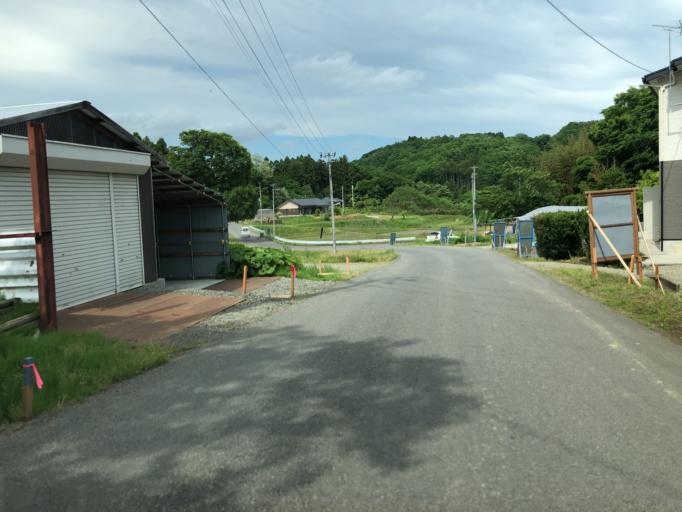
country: JP
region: Fukushima
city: Nihommatsu
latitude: 37.6387
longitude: 140.5229
